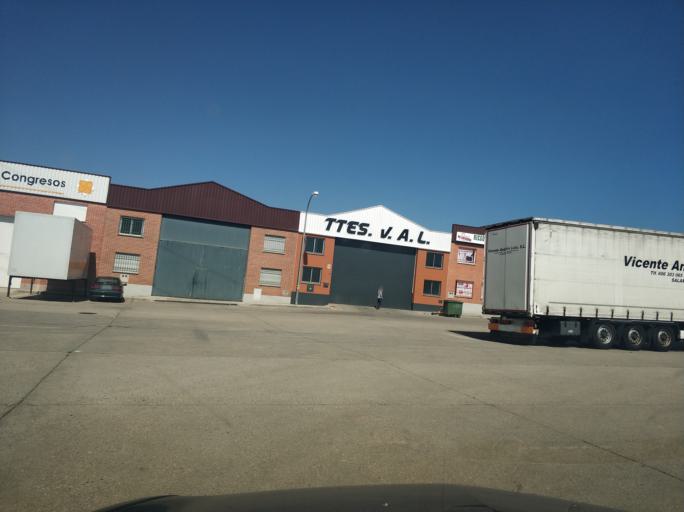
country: ES
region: Castille and Leon
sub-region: Provincia de Salamanca
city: Villares de la Reina
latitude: 40.9936
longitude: -5.6326
